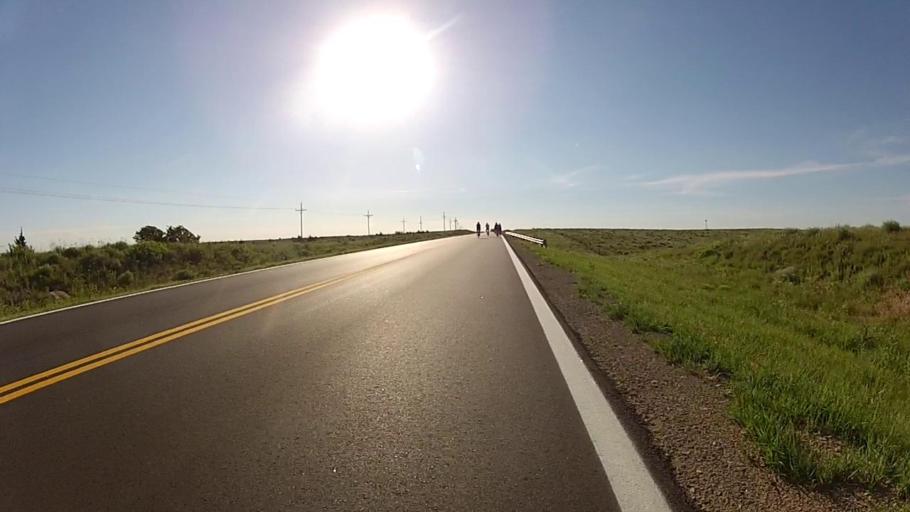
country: US
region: Kansas
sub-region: Comanche County
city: Coldwater
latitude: 37.2804
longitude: -99.0178
